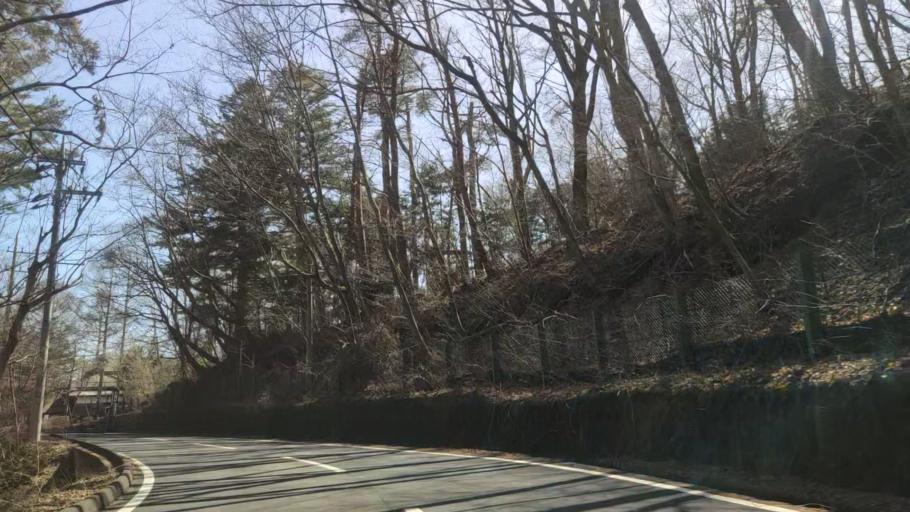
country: JP
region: Yamanashi
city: Fujikawaguchiko
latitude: 35.4590
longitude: 138.8184
